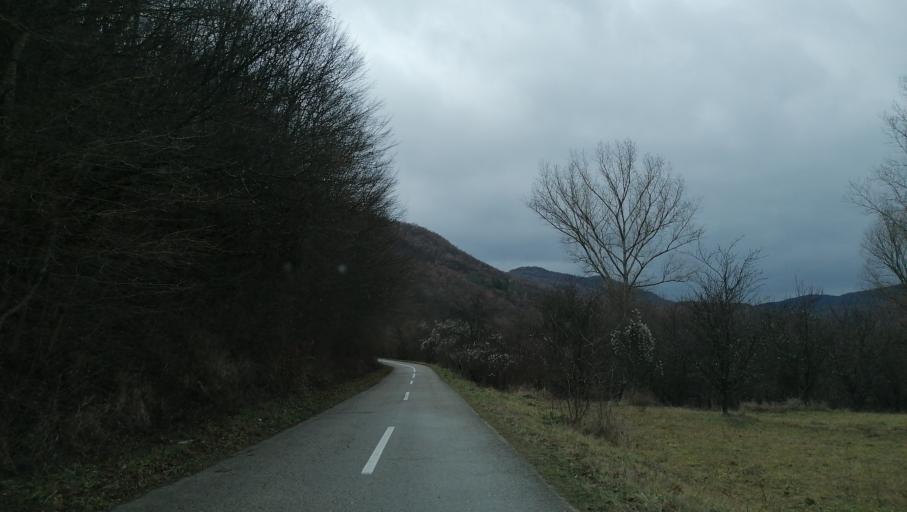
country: RS
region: Central Serbia
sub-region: Pirotski Okrug
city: Dimitrovgrad
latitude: 42.9338
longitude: 22.7742
